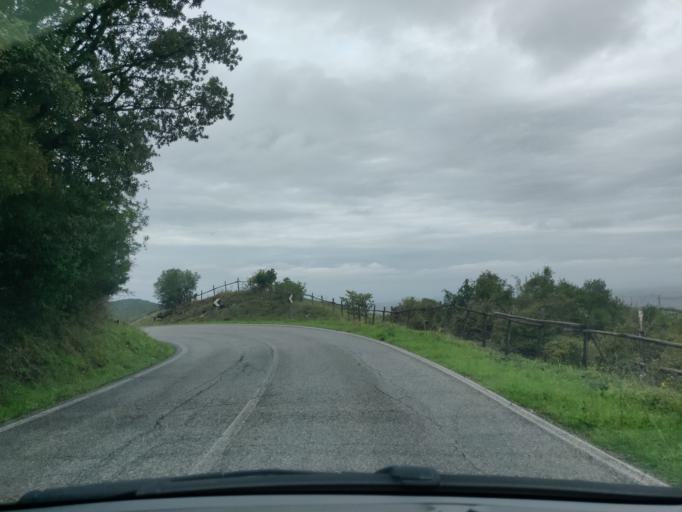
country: IT
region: Latium
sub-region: Citta metropolitana di Roma Capitale
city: Allumiere
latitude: 42.1454
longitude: 11.8807
